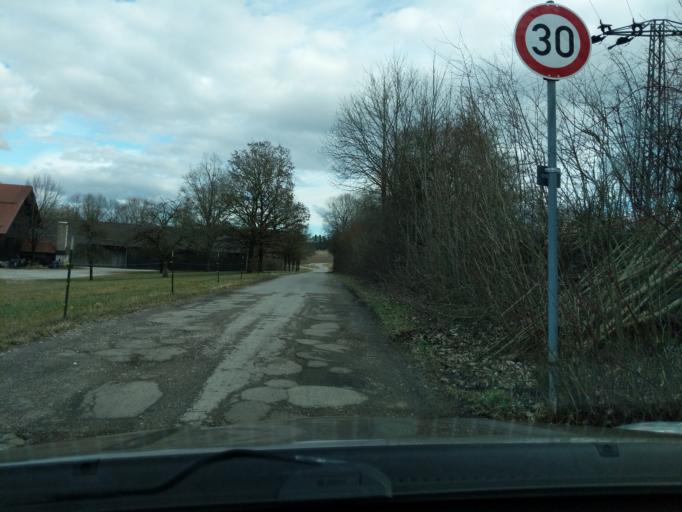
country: DE
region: Bavaria
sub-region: Upper Bavaria
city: Kirchseeon
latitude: 48.0649
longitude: 11.9172
